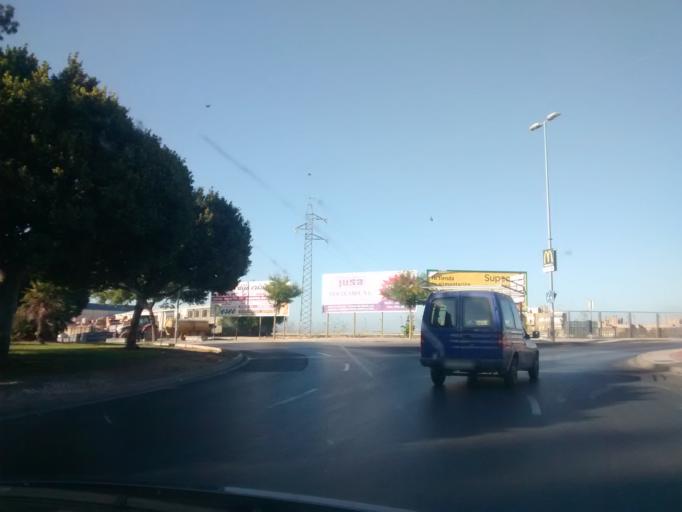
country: ES
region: Andalusia
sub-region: Provincia de Cadiz
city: Jerez de la Frontera
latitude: 36.6734
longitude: -6.1225
